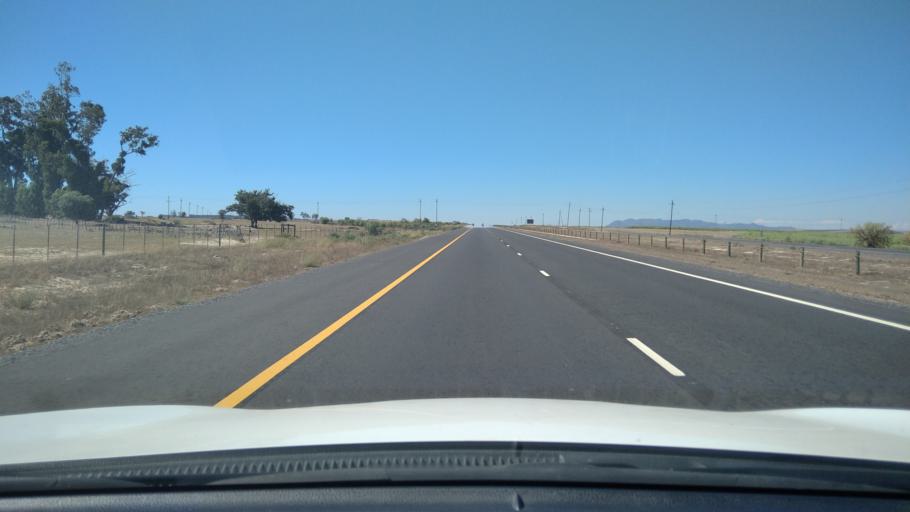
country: ZA
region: Western Cape
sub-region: West Coast District Municipality
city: Malmesbury
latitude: -33.5581
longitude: 18.6273
